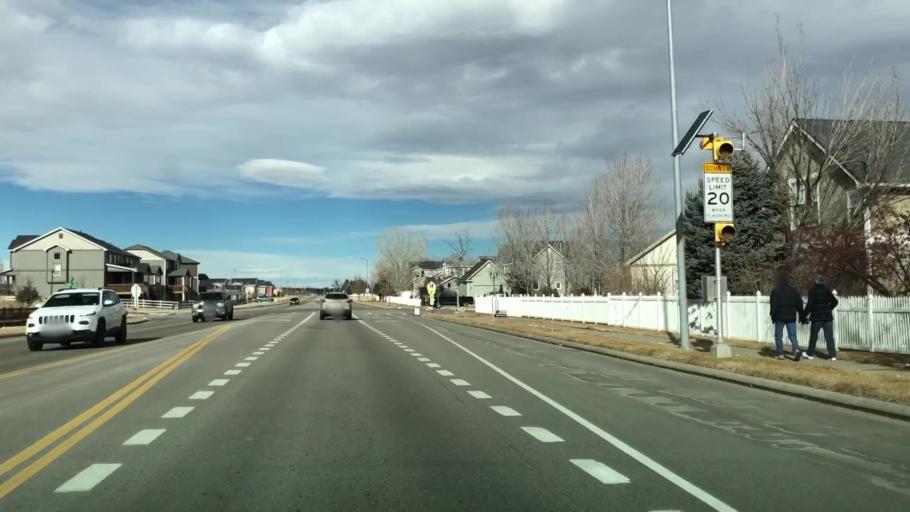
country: US
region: Colorado
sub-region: Weld County
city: Windsor
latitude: 40.4847
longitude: -104.9264
